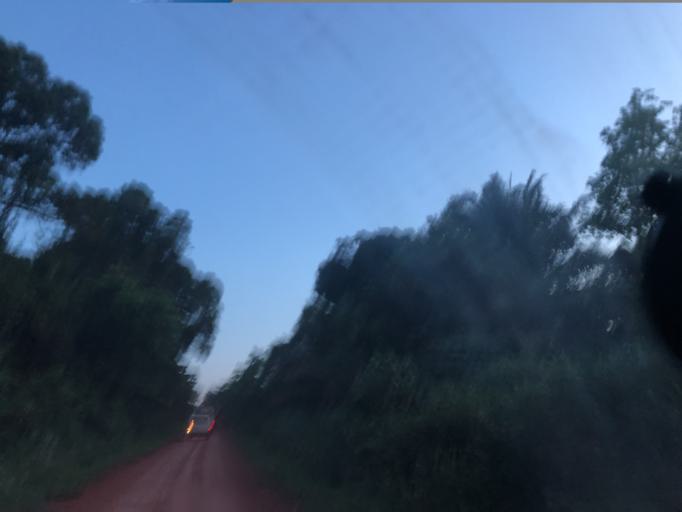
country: CD
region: Equateur
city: Libenge
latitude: 3.9023
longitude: 18.6938
